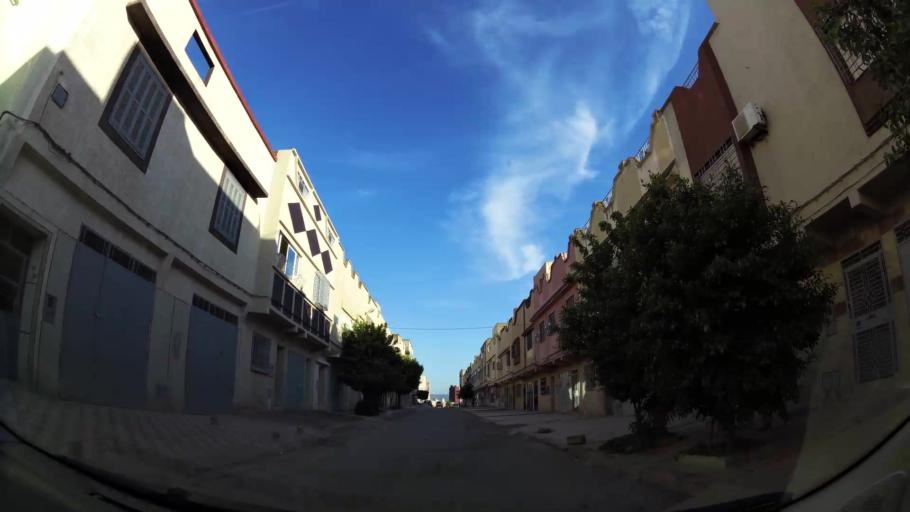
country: MA
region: Oriental
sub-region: Oujda-Angad
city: Oujda
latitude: 34.6983
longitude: -1.9058
